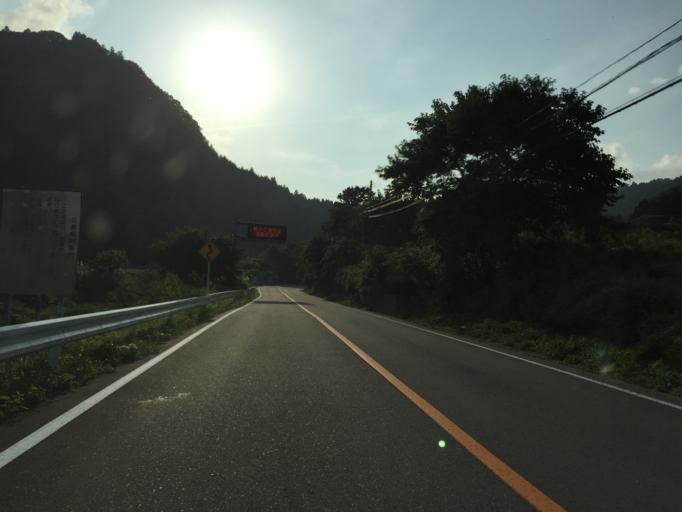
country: JP
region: Fukushima
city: Namie
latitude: 37.5071
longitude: 140.9244
